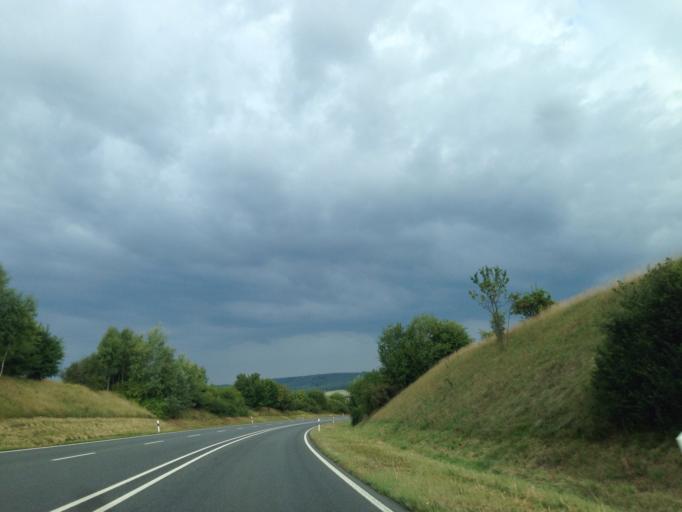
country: DE
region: Thuringia
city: Neustadt (Orla)
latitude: 50.7249
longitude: 11.7338
